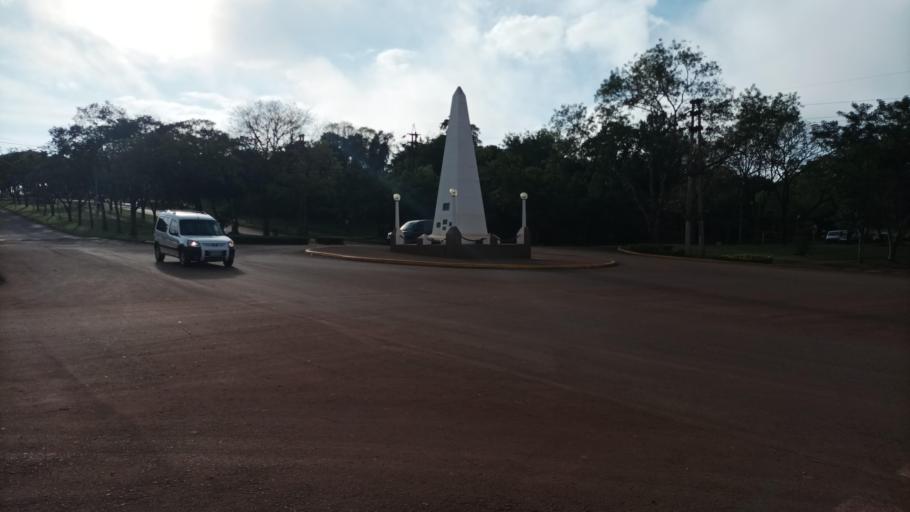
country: AR
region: Misiones
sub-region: Departamento de Apostoles
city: Apostoles
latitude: -27.9110
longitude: -55.7589
